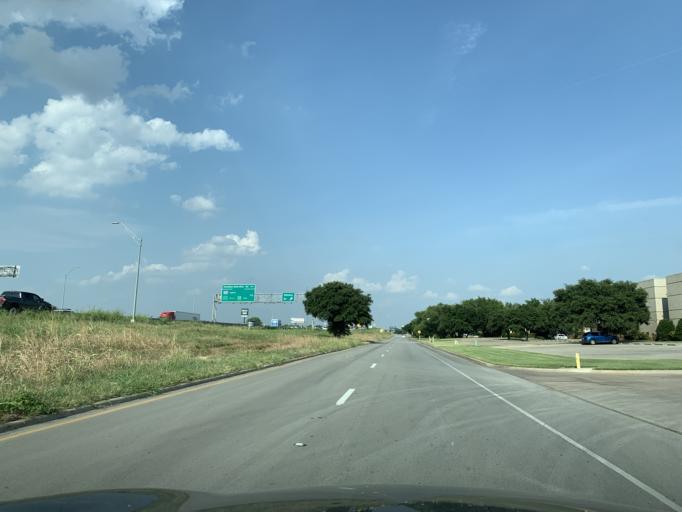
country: US
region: Texas
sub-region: Tarrant County
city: Haltom City
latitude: 32.7905
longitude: -97.2493
